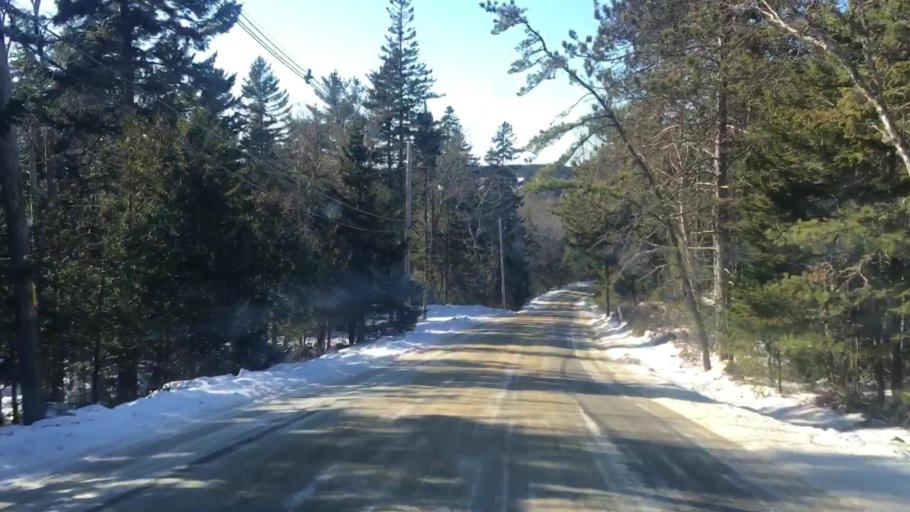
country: US
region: Maine
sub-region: Hancock County
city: Castine
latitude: 44.3400
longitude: -68.7310
